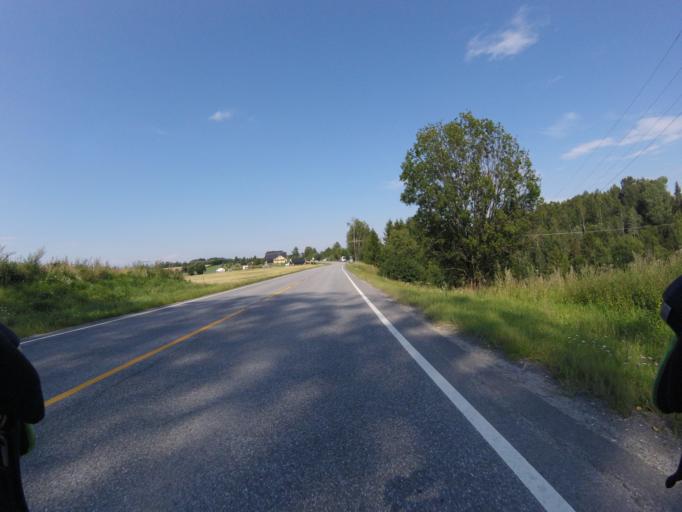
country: NO
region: Akershus
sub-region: Sorum
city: Frogner
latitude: 60.0479
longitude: 11.1188
